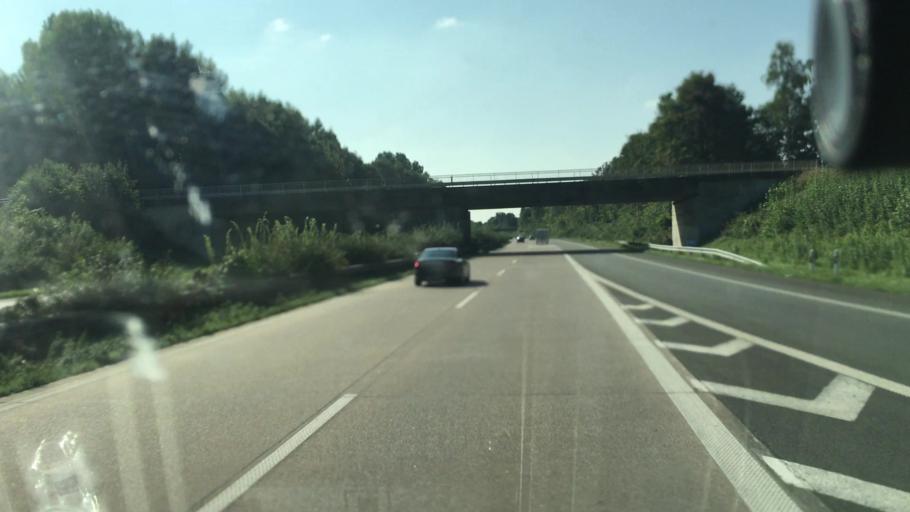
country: DE
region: Lower Saxony
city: Rastede
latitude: 53.2440
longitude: 8.1759
